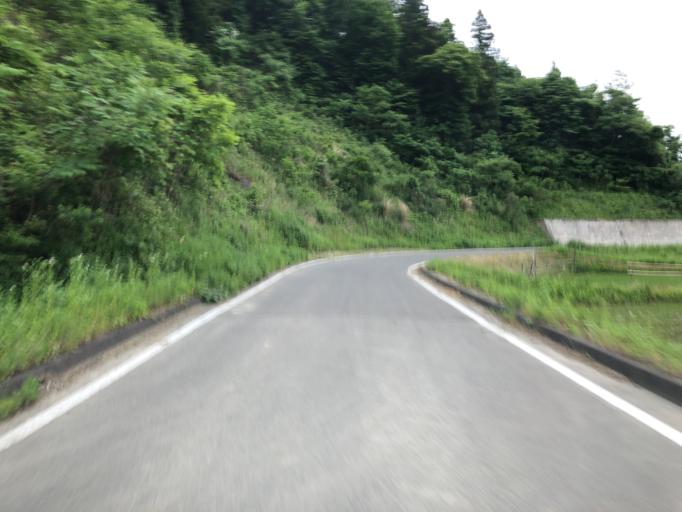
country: JP
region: Fukushima
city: Funehikimachi-funehiki
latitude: 37.4526
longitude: 140.5298
